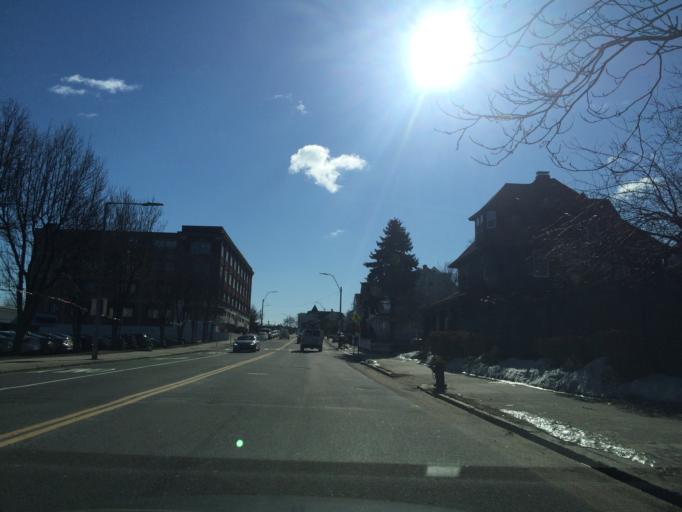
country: US
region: Massachusetts
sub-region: Norfolk County
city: Brookline
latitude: 42.3544
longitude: -71.1425
